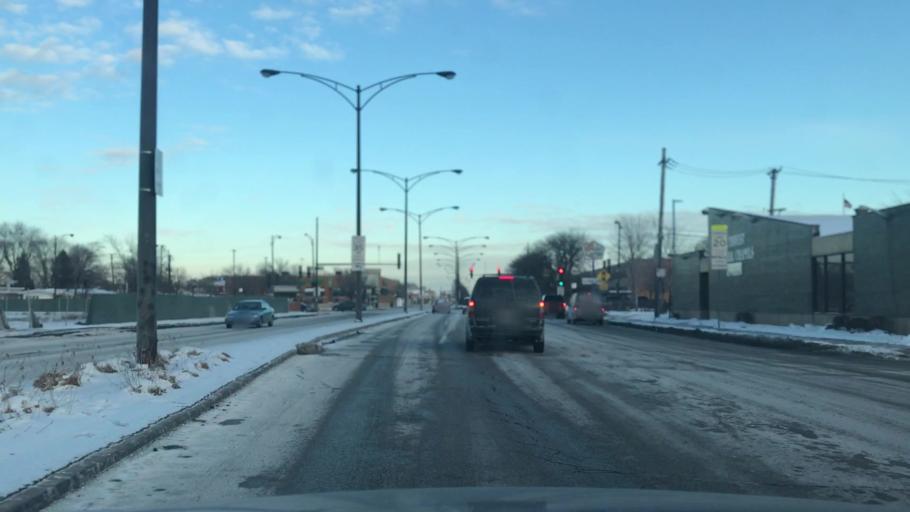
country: US
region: Illinois
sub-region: Cook County
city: Hometown
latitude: 41.7495
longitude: -87.7233
